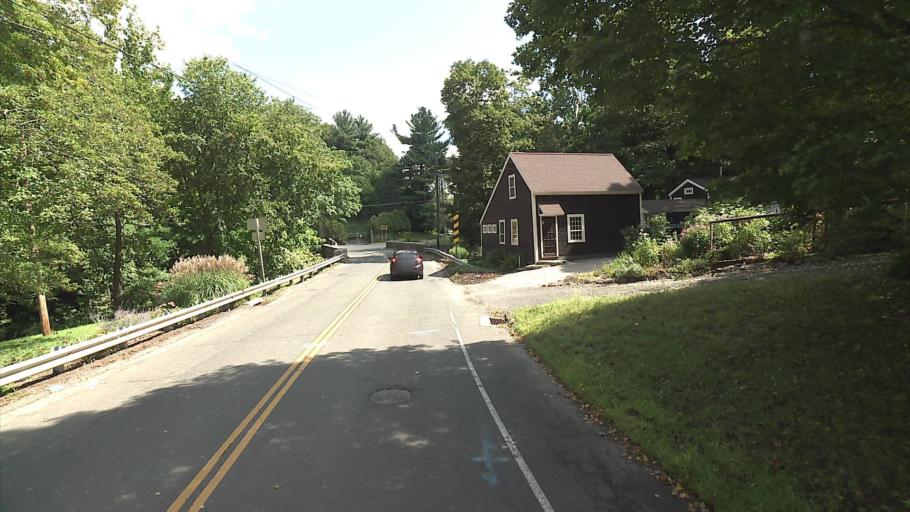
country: US
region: Connecticut
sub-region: Hartford County
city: Glastonbury Center
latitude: 41.6669
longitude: -72.6085
